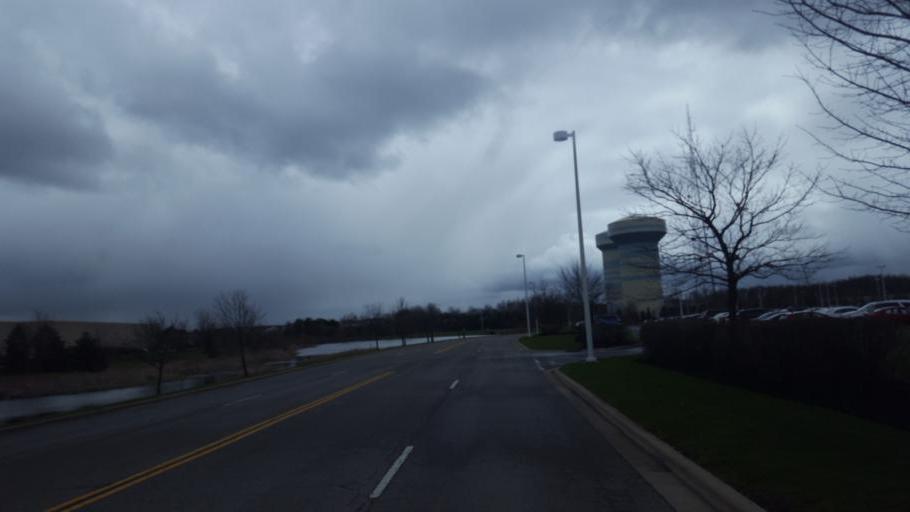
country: US
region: Ohio
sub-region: Franklin County
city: Worthington
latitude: 40.1404
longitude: -82.9937
